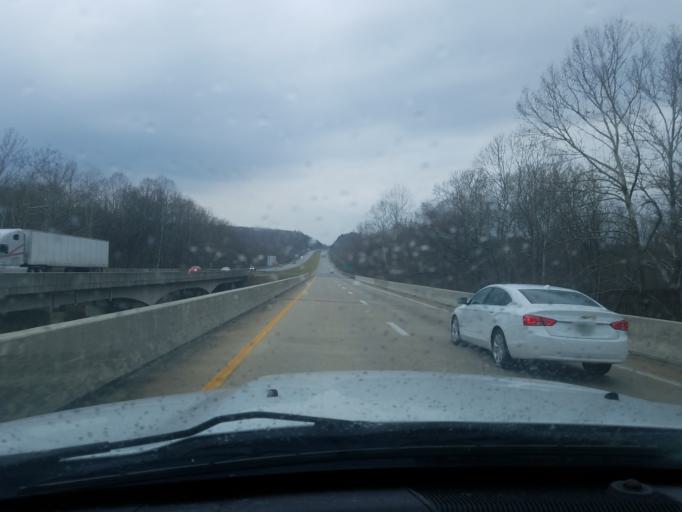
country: US
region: Kentucky
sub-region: Rowan County
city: Morehead
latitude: 38.1879
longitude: -83.4941
